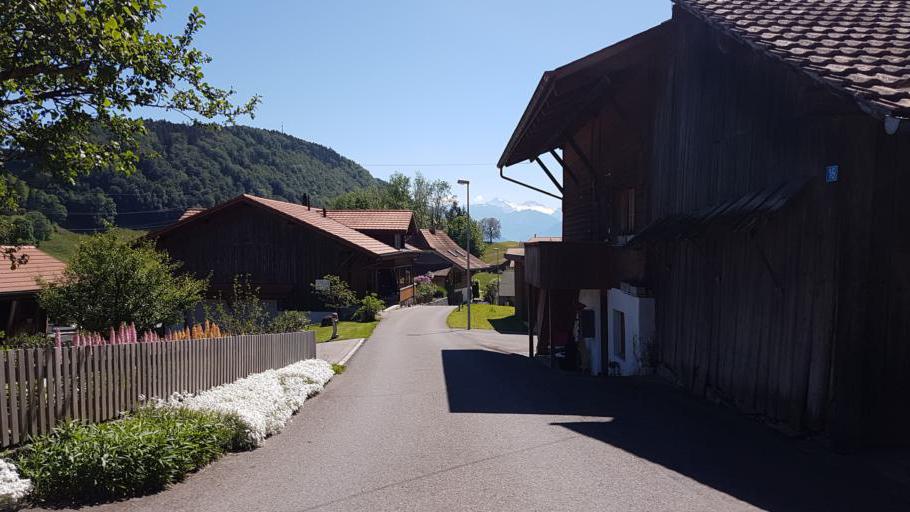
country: CH
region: Bern
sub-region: Thun District
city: Thierachern
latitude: 46.7103
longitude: 7.5744
